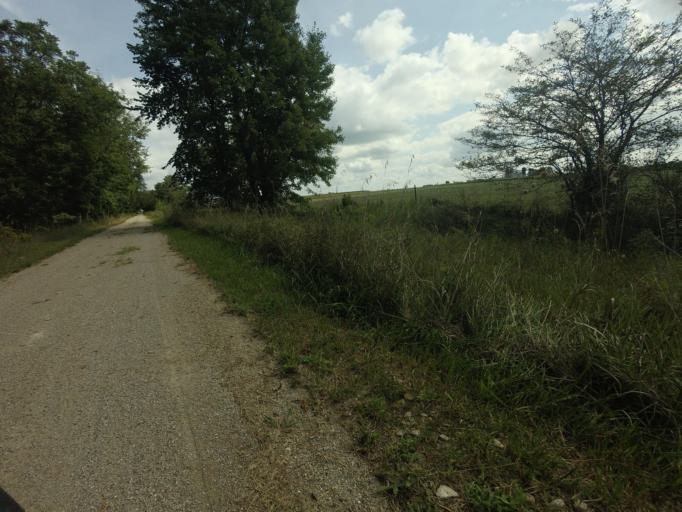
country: CA
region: Ontario
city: North Perth
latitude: 43.5706
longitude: -80.8866
